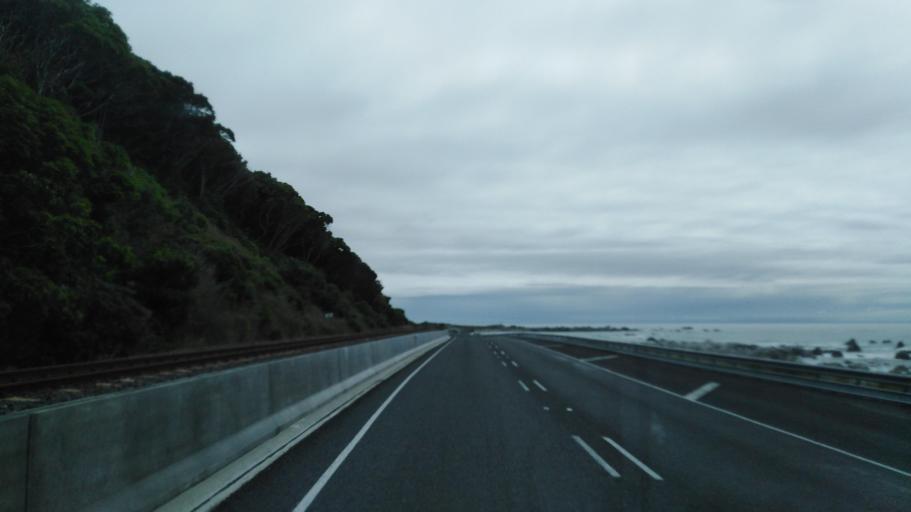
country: NZ
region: Canterbury
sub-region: Kaikoura District
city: Kaikoura
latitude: -42.2416
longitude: 173.8370
